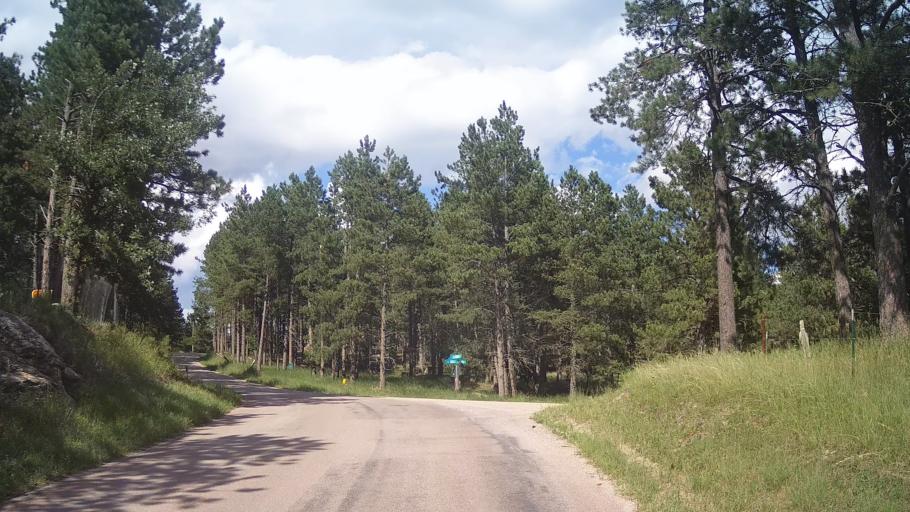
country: US
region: South Dakota
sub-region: Pennington County
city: Colonial Pine Hills
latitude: 43.8488
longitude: -103.3834
